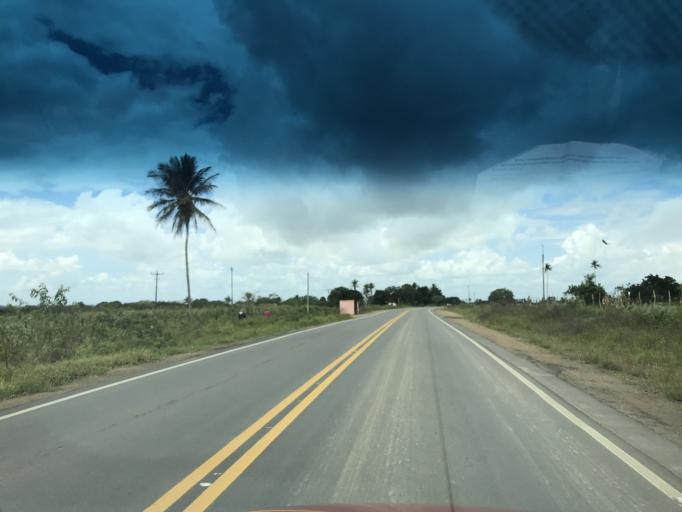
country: BR
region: Bahia
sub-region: Conceicao Do Almeida
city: Conceicao do Almeida
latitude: -12.6950
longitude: -39.2437
